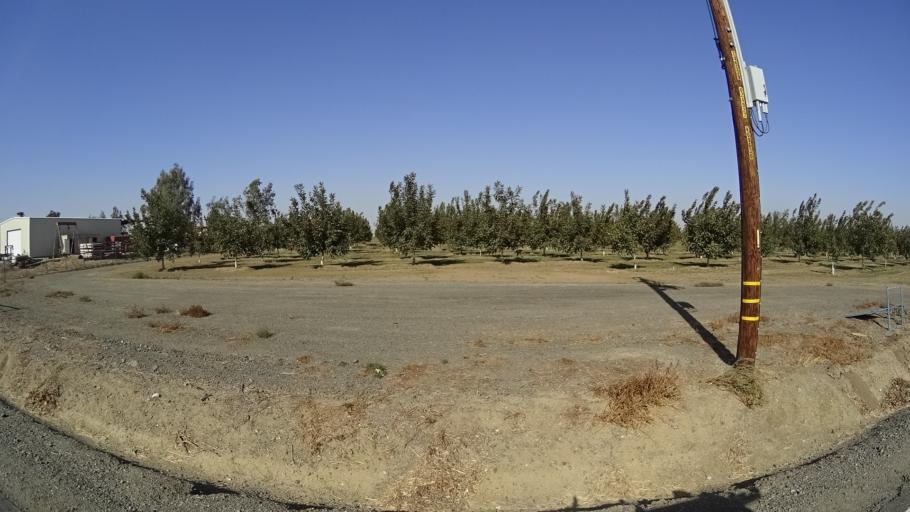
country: US
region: California
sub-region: Yolo County
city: Cottonwood
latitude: 38.7188
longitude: -121.9525
